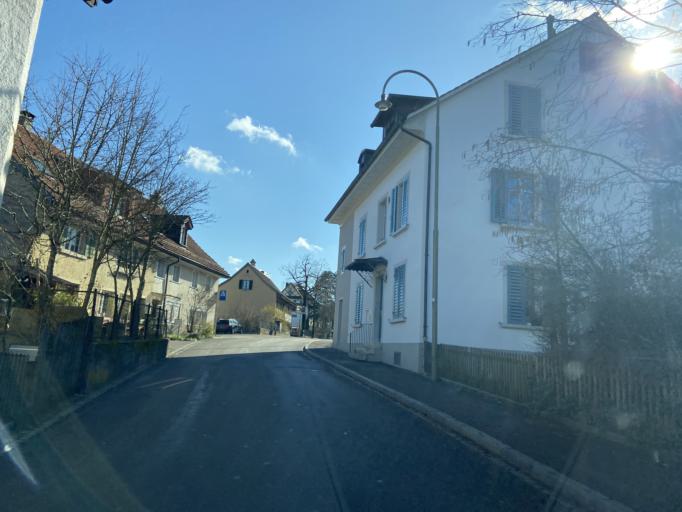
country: CH
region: Zurich
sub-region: Bezirk Winterthur
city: Wuelflingen (Kreis 6) / Lindenplatz
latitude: 47.5094
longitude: 8.6954
